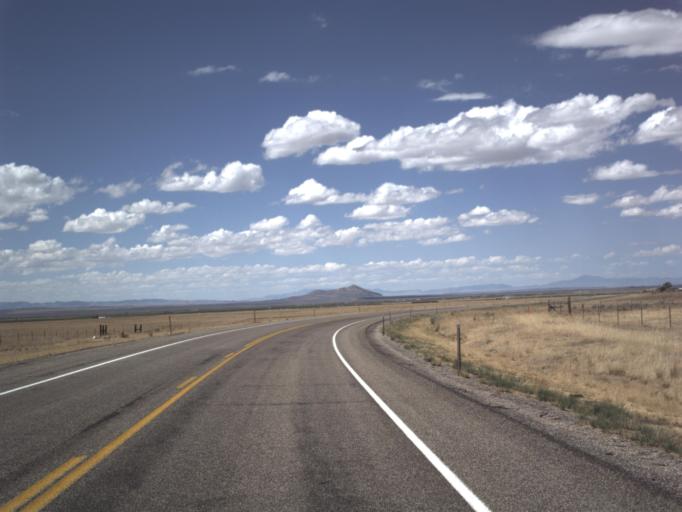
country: US
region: Utah
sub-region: Millard County
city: Fillmore
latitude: 39.1144
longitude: -112.3032
